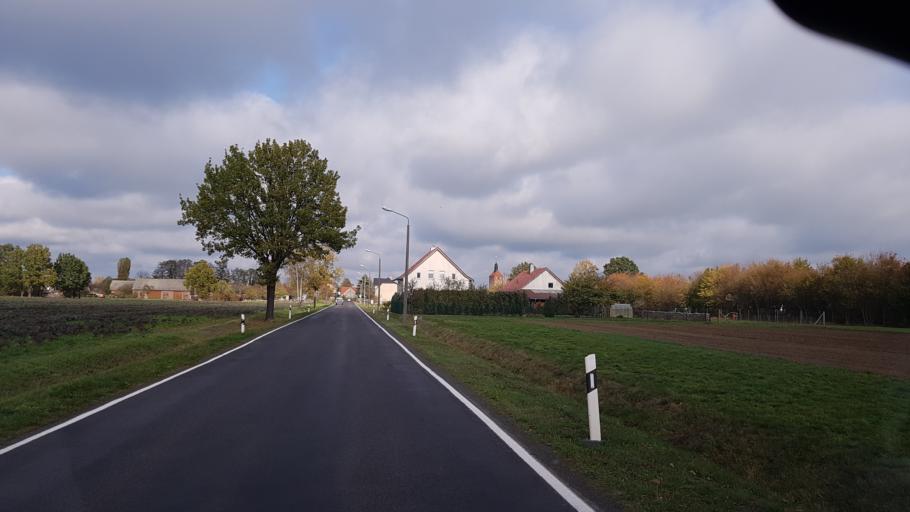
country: DE
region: Brandenburg
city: Schonewalde
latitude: 51.6554
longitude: 13.5889
